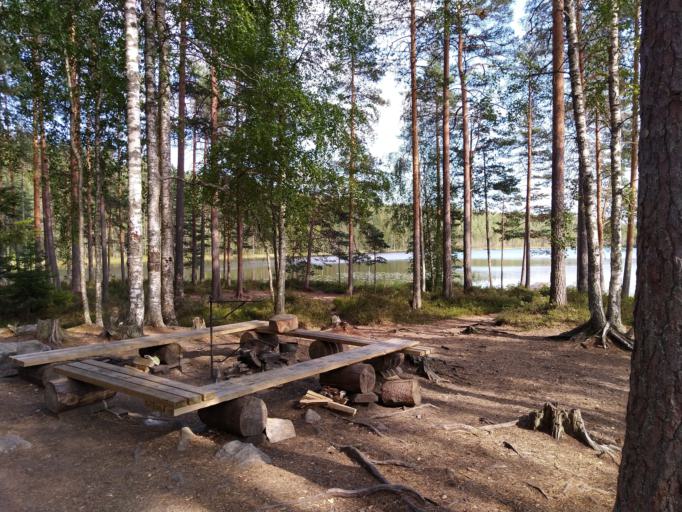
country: FI
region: Pirkanmaa
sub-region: Tampere
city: Kuru
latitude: 62.0438
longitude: 23.8211
